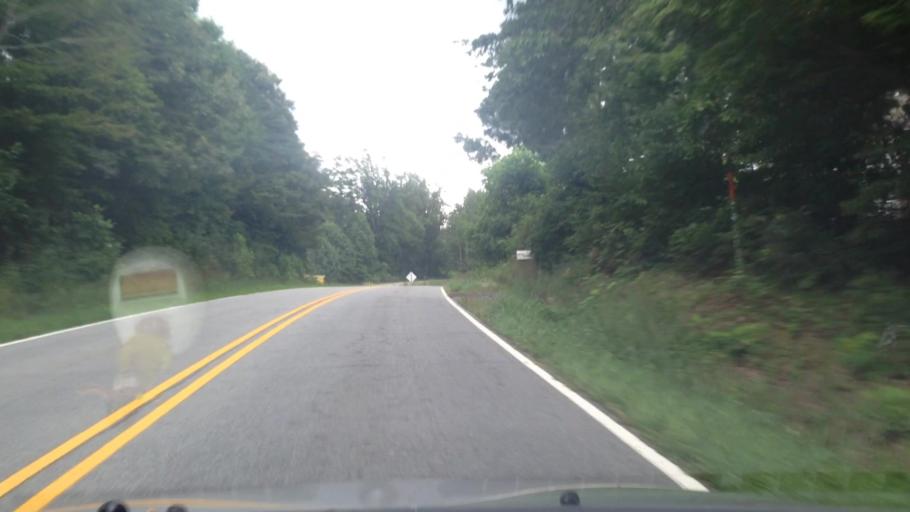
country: US
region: North Carolina
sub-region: Forsyth County
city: Walkertown
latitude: 36.2030
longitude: -80.1672
